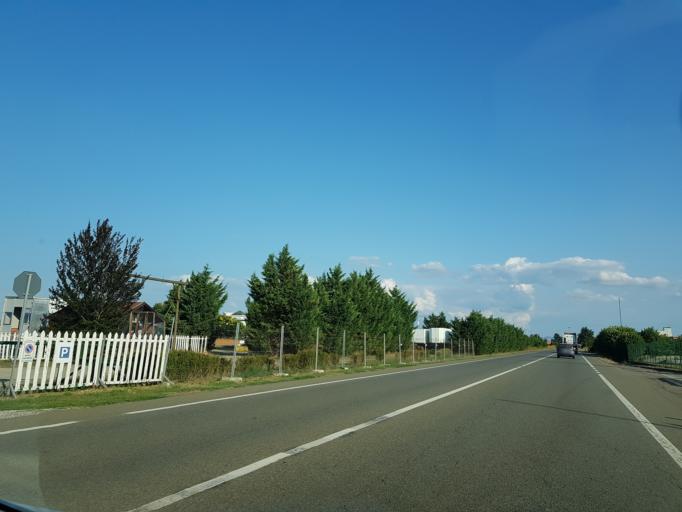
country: IT
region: Piedmont
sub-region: Provincia di Alessandria
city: Mandrogne
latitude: 44.8425
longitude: 8.7284
